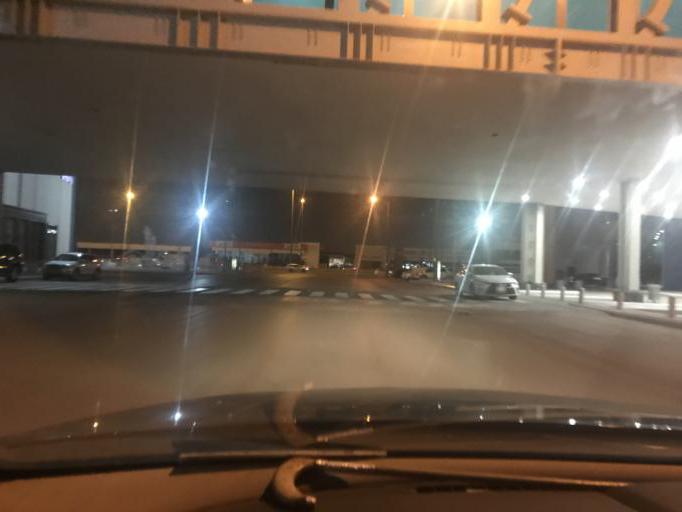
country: SA
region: Ar Riyad
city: Riyadh
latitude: 24.7384
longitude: 46.7975
